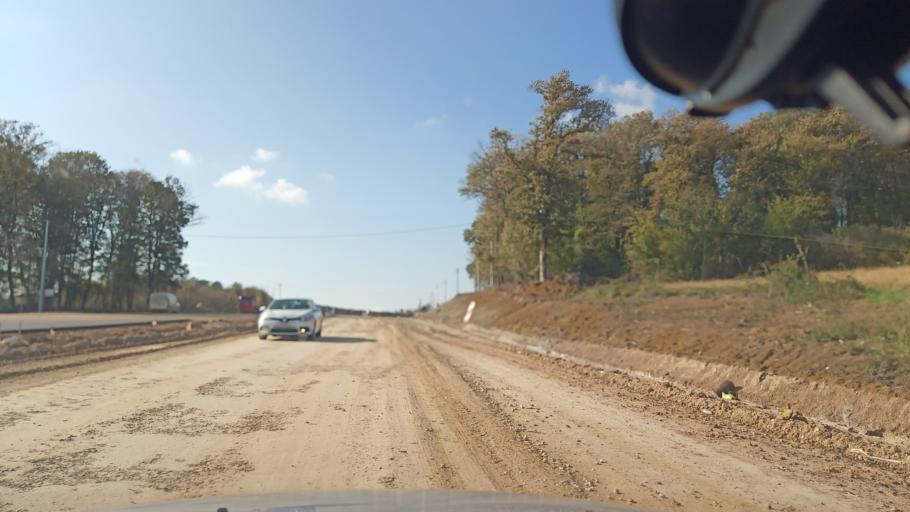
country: TR
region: Sakarya
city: Ferizli
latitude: 41.0996
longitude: 30.4713
